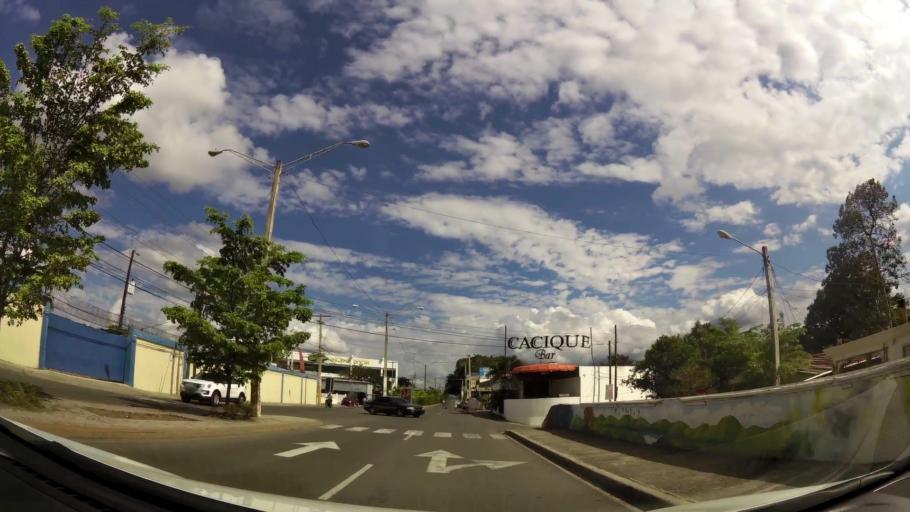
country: DO
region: La Vega
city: Concepcion de La Vega
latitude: 19.2279
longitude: -70.5254
